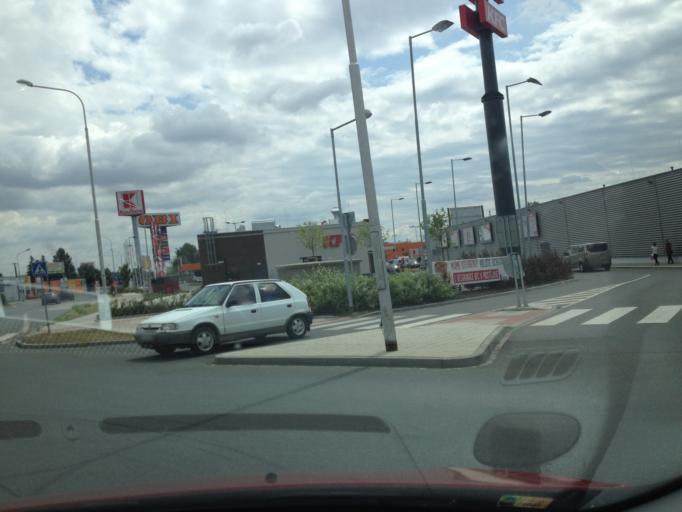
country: CZ
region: Olomoucky
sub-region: Okres Prostejov
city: Prostejov
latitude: 49.4838
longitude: 17.1224
